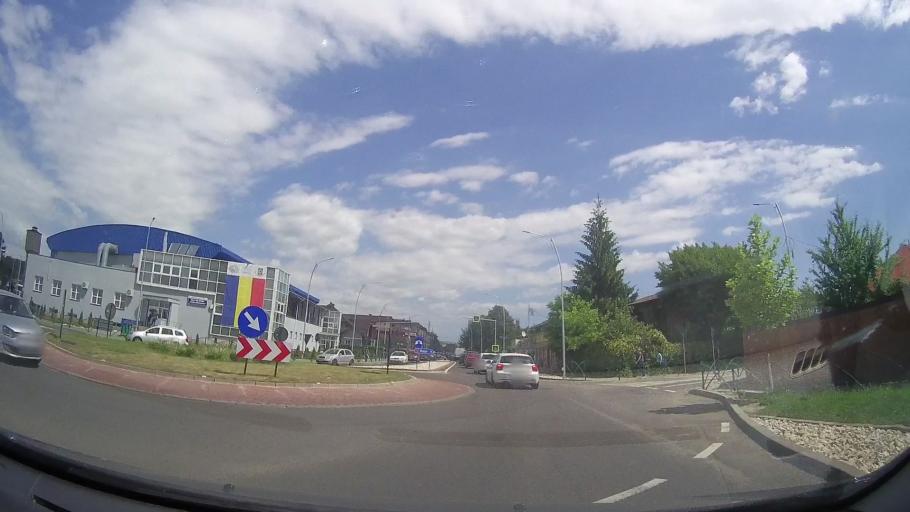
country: RO
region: Prahova
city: Valenii de Munte
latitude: 45.1792
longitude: 26.0358
